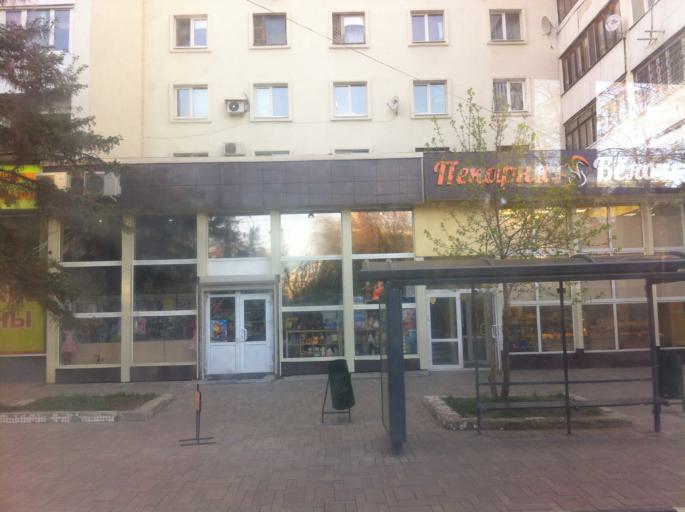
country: RU
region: Samara
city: Samara
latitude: 53.2014
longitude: 50.1114
